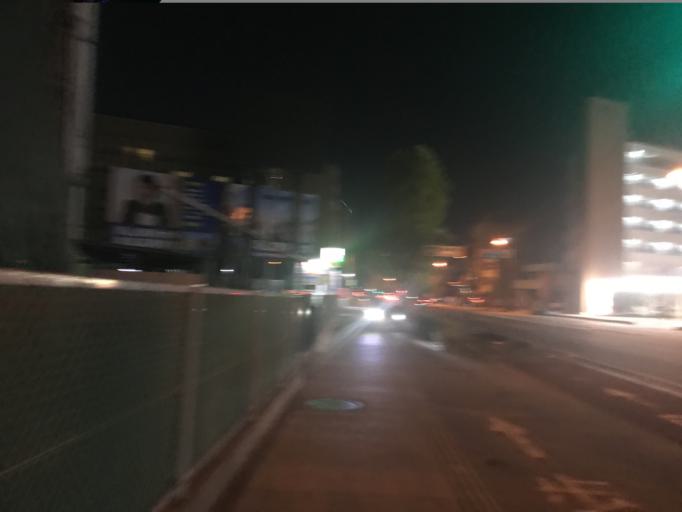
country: JP
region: Okayama
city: Okayama-shi
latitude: 34.6750
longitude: 133.9205
